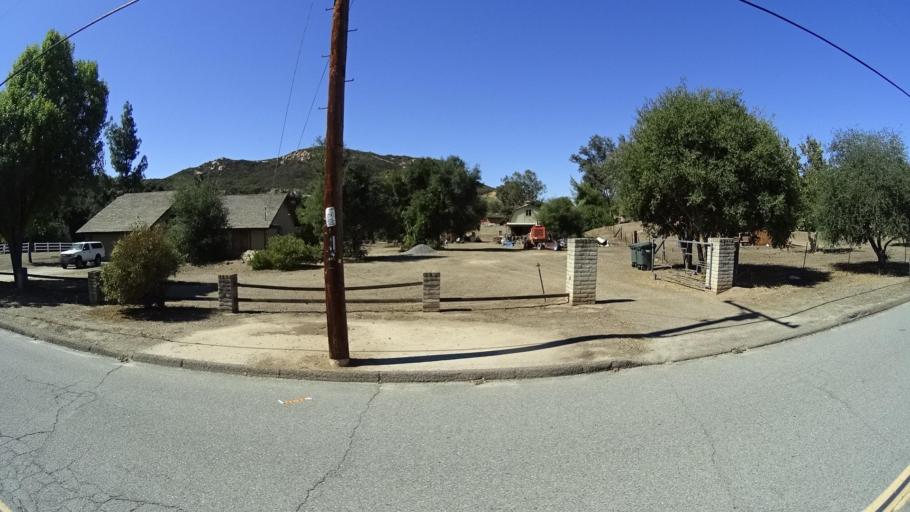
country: US
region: California
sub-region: San Diego County
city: Alpine
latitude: 32.7511
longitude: -116.7596
